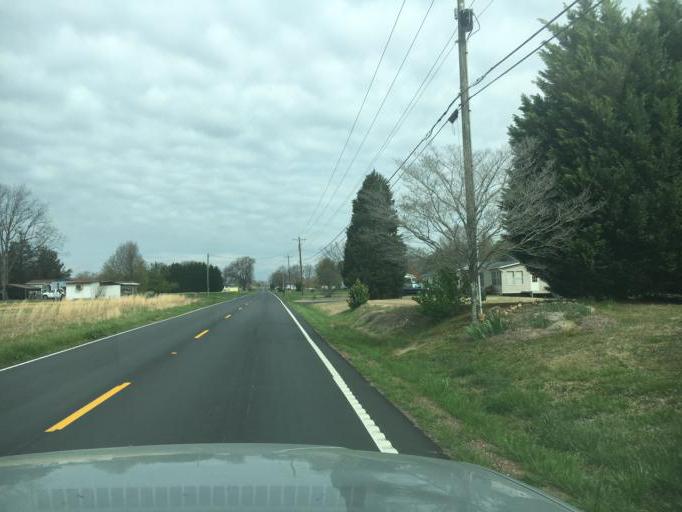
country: US
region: South Carolina
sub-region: Spartanburg County
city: Inman Mills
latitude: 35.0439
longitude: -82.1347
